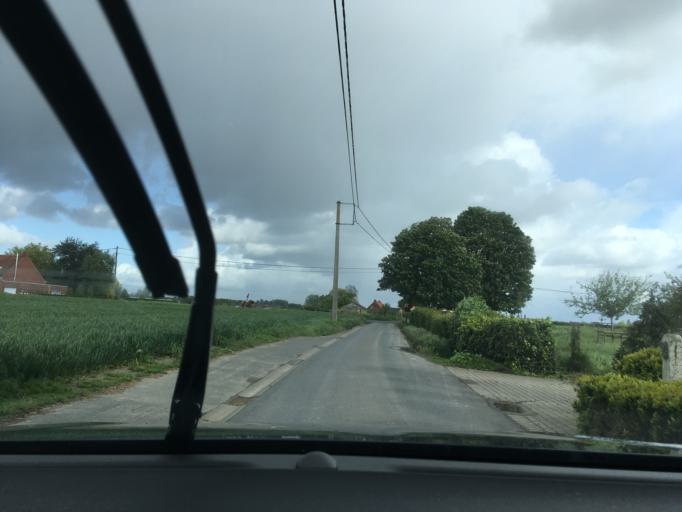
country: BE
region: Flanders
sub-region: Provincie West-Vlaanderen
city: Hooglede
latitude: 51.0078
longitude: 3.0755
